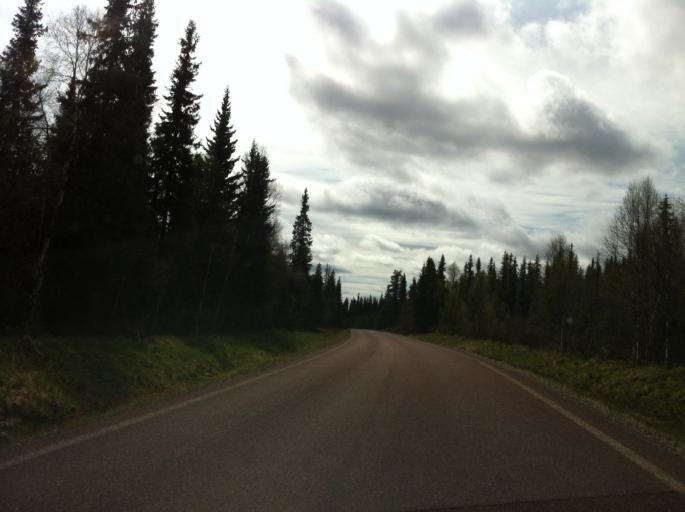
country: NO
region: Hedmark
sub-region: Engerdal
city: Engerdal
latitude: 62.1578
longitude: 12.9480
